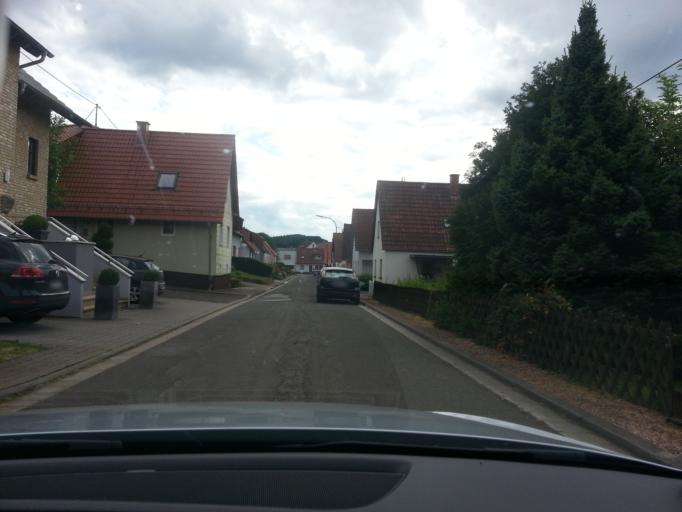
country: DE
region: Saarland
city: Marpingen
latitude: 49.4464
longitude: 7.0545
